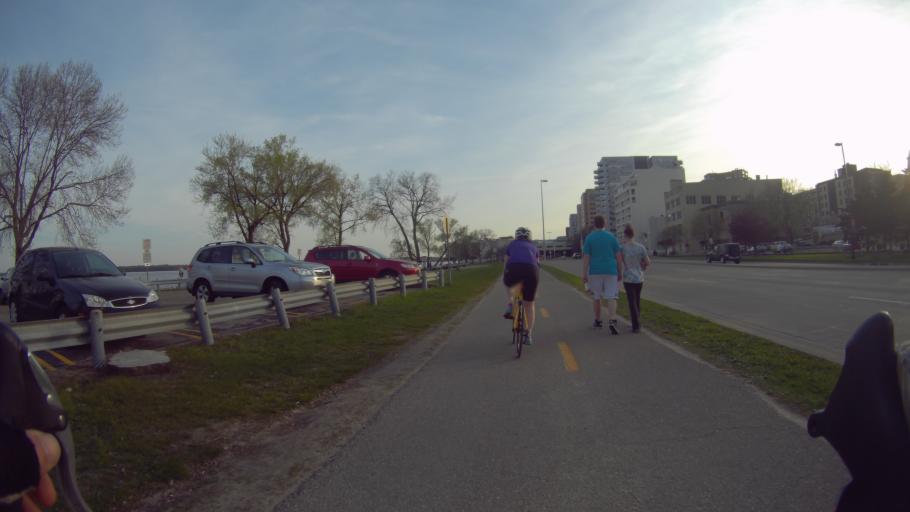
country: US
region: Wisconsin
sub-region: Dane County
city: Madison
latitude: 43.0753
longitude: -89.3759
